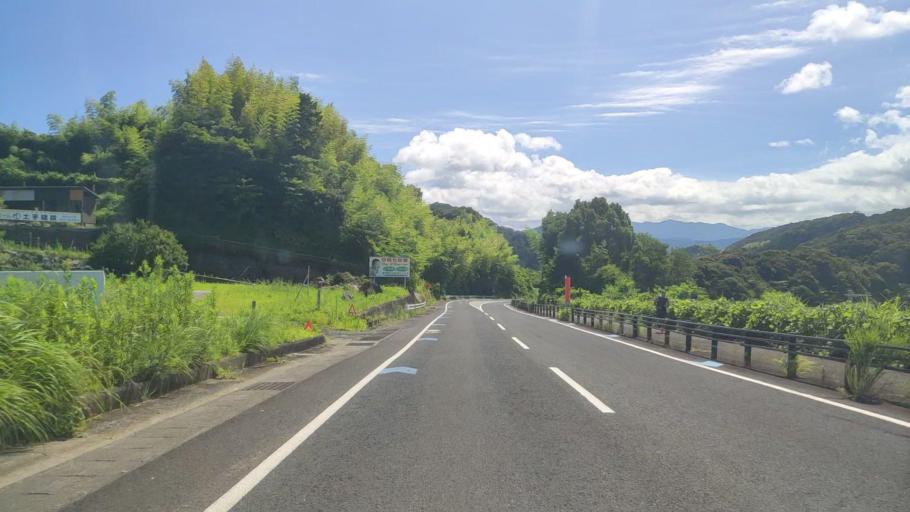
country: JP
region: Wakayama
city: Shingu
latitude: 33.7433
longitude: 136.0081
